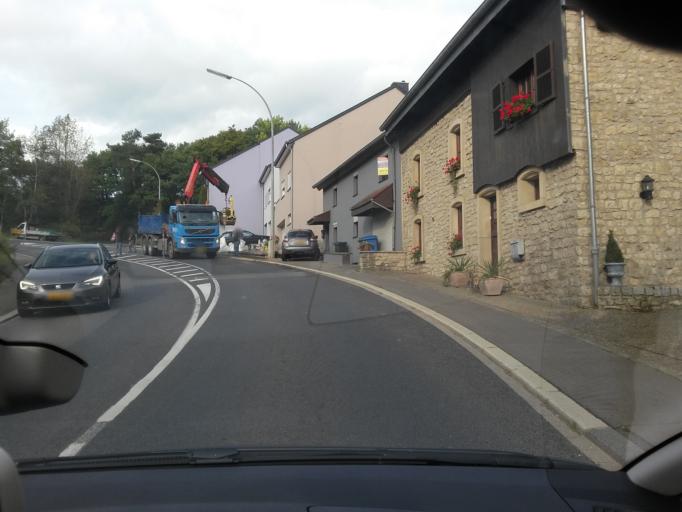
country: LU
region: Luxembourg
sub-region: Canton de Capellen
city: Hobscheid
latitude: 49.6951
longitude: 5.9193
